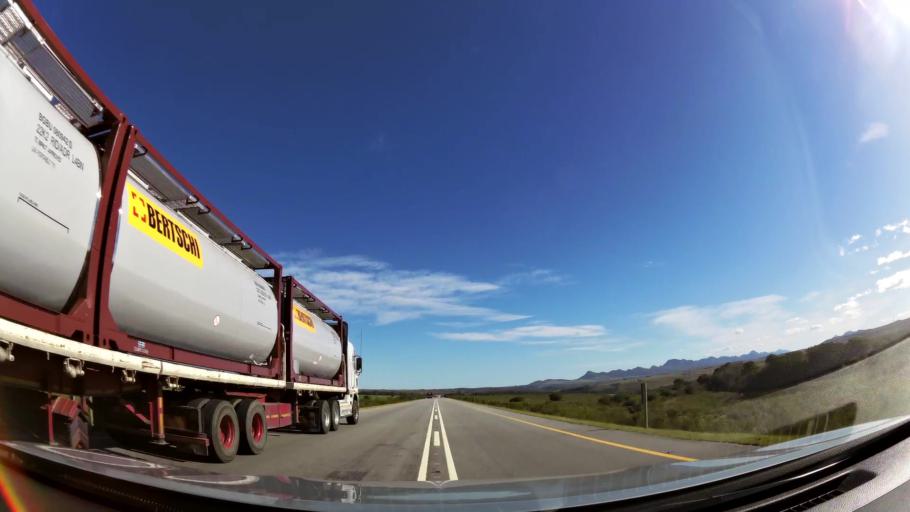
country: ZA
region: Eastern Cape
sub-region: Cacadu District Municipality
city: Kruisfontein
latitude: -34.0215
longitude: 24.6155
